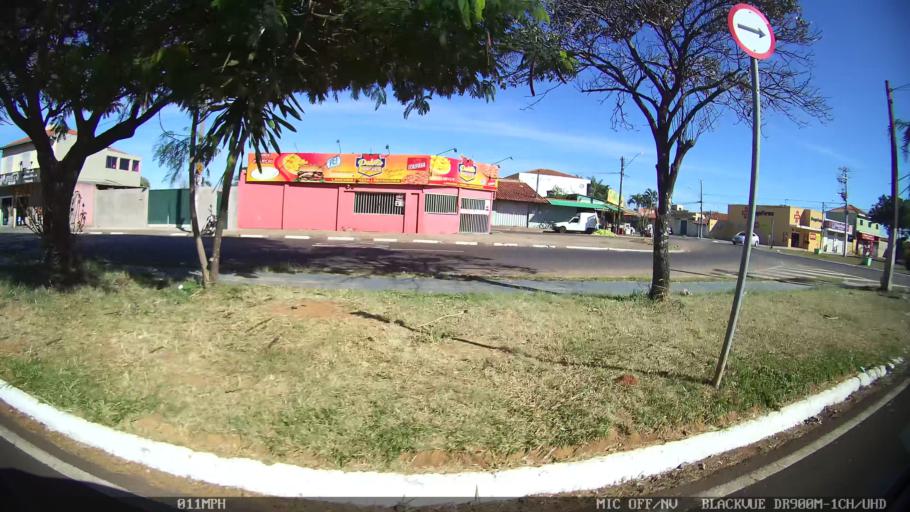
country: BR
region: Sao Paulo
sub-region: Franca
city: Franca
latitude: -20.5545
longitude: -47.3602
